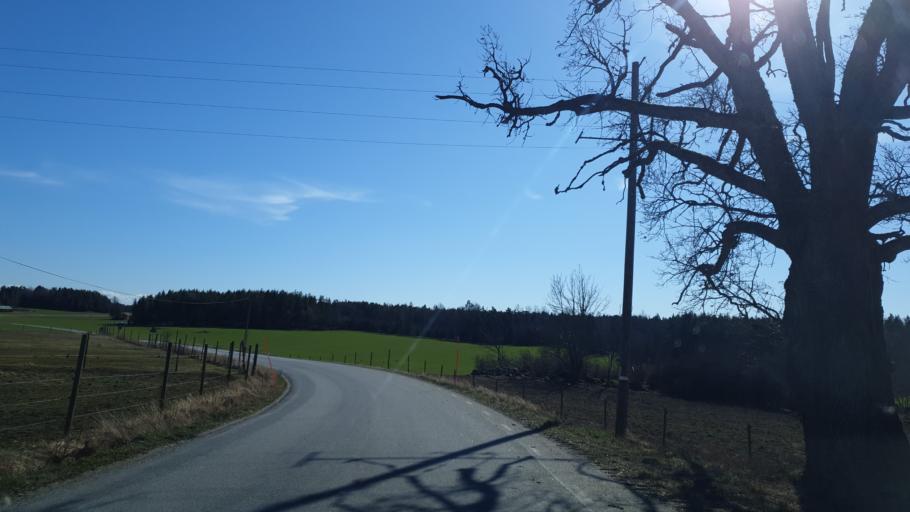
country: SE
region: Uppsala
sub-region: Enkopings Kommun
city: Dalby
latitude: 59.5564
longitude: 17.3148
